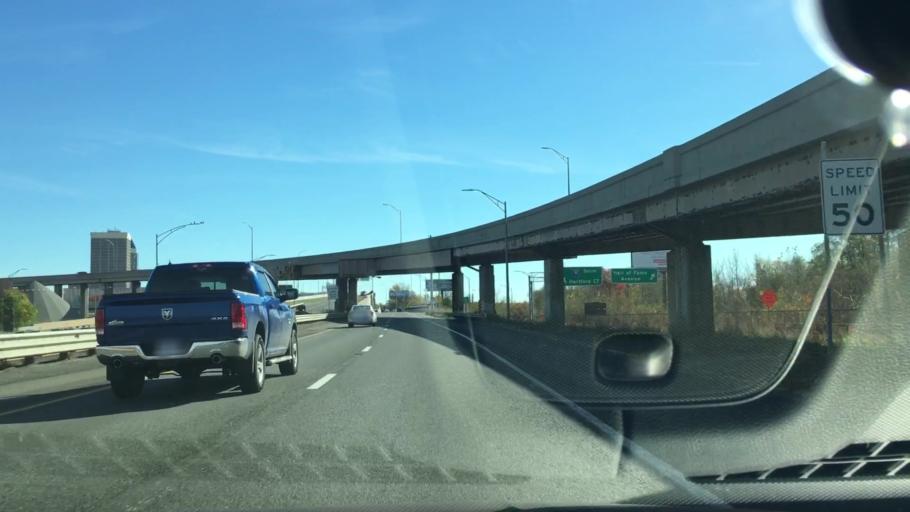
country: US
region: Massachusetts
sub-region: Hampden County
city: Springfield
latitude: 42.1086
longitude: -72.6041
